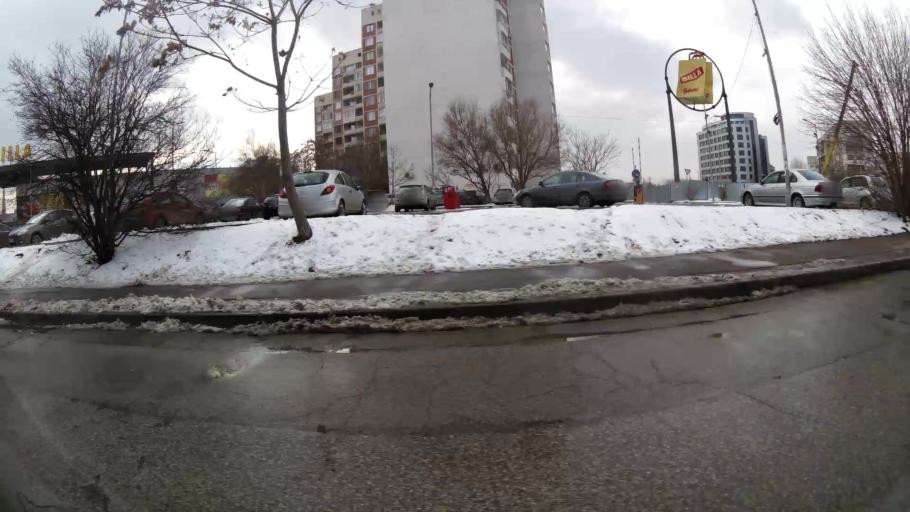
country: BG
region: Sofia-Capital
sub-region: Stolichna Obshtina
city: Sofia
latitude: 42.7028
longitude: 23.3537
